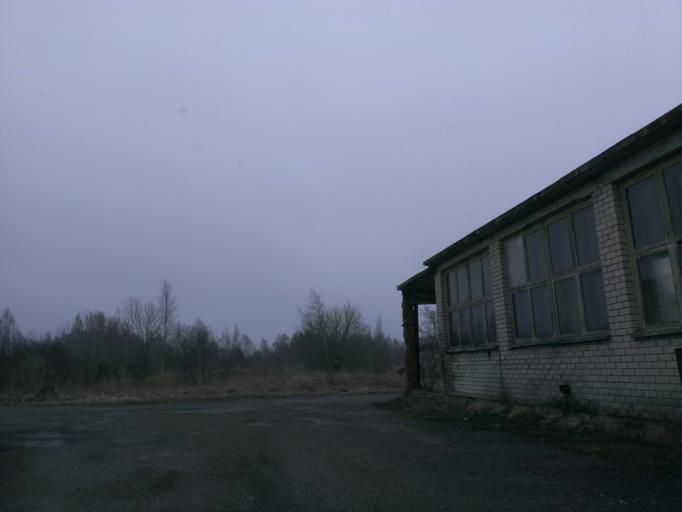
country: EE
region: Laeaene
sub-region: Lihula vald
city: Lihula
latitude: 58.5875
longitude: 23.5251
